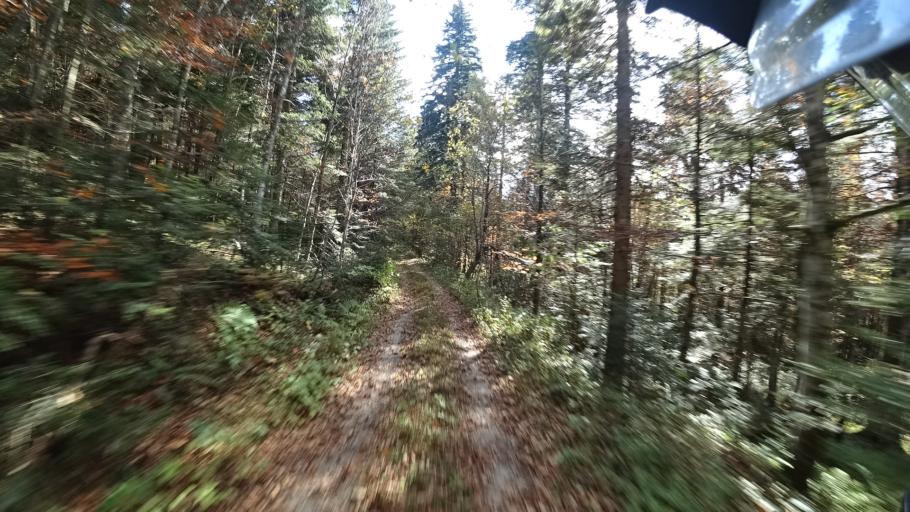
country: HR
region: Karlovacka
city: Plaski
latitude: 45.0669
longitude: 15.3144
